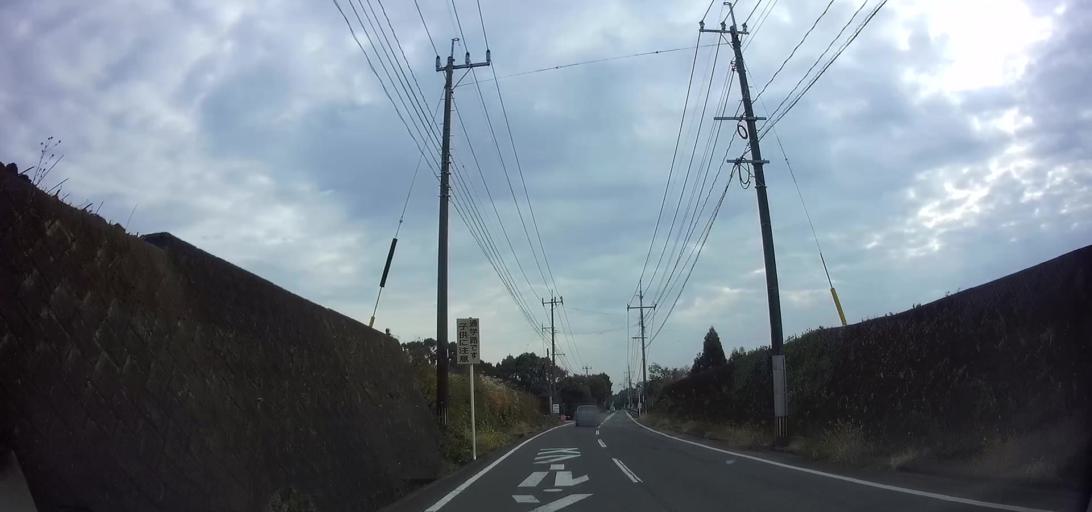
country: JP
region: Nagasaki
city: Shimabara
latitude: 32.6925
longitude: 130.3015
